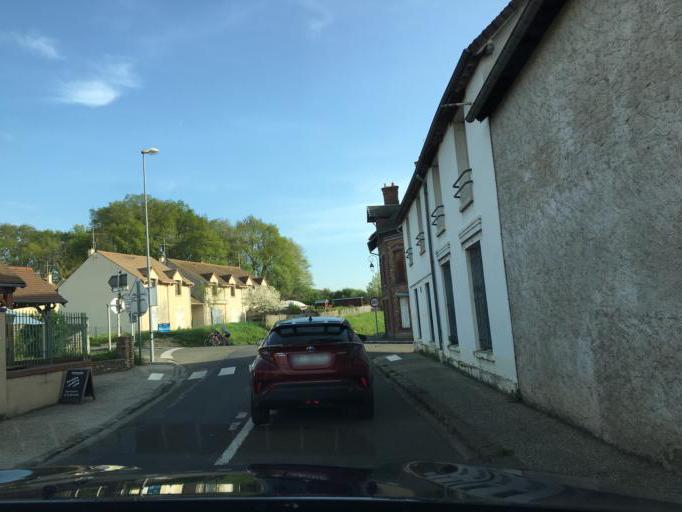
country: FR
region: Centre
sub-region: Departement d'Eure-et-Loir
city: Epernon
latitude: 48.6504
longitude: 1.6887
